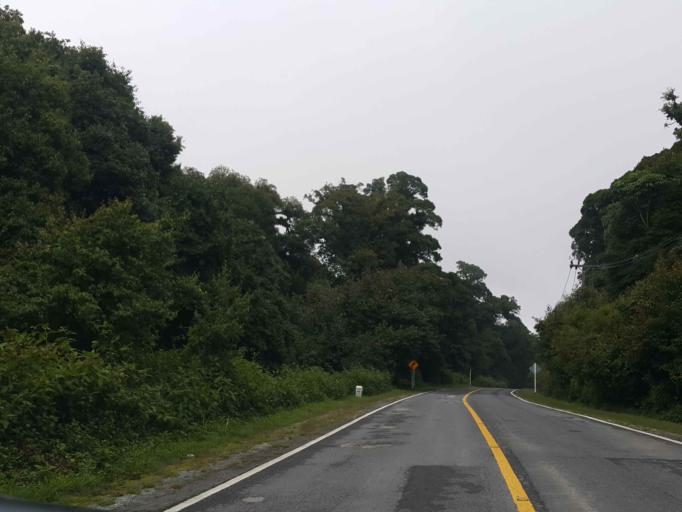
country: TH
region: Chiang Mai
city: Mae Chaem
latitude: 18.5805
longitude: 98.4807
